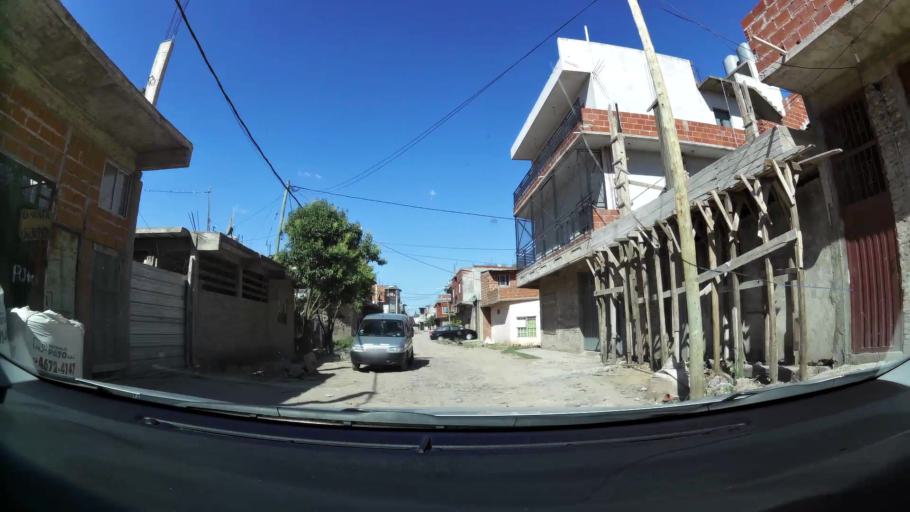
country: AR
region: Buenos Aires F.D.
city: Villa Lugano
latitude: -34.7098
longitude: -58.4773
